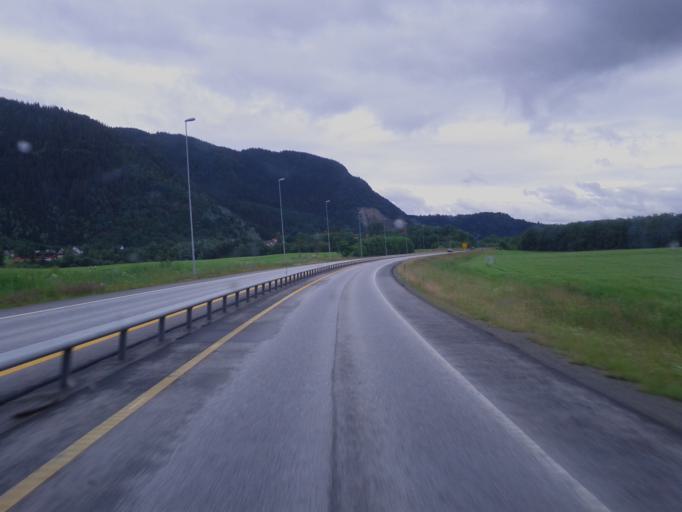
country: NO
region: Sor-Trondelag
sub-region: Melhus
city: Melhus
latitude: 63.2744
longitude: 10.2866
